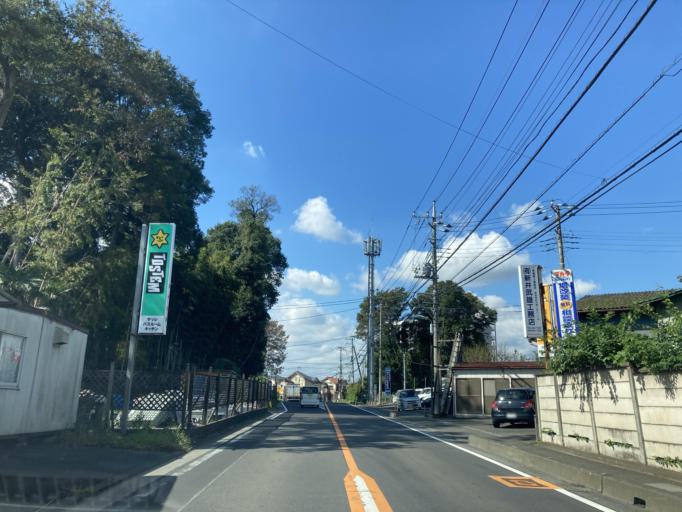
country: JP
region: Saitama
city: Tokorozawa
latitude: 35.8111
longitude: 139.4993
